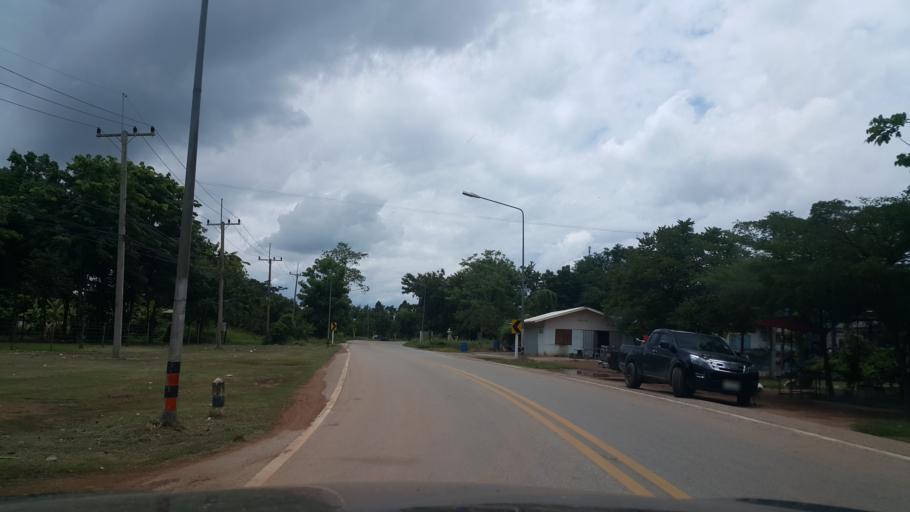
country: TH
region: Sukhothai
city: Kong Krailat
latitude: 16.9070
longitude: 99.8805
